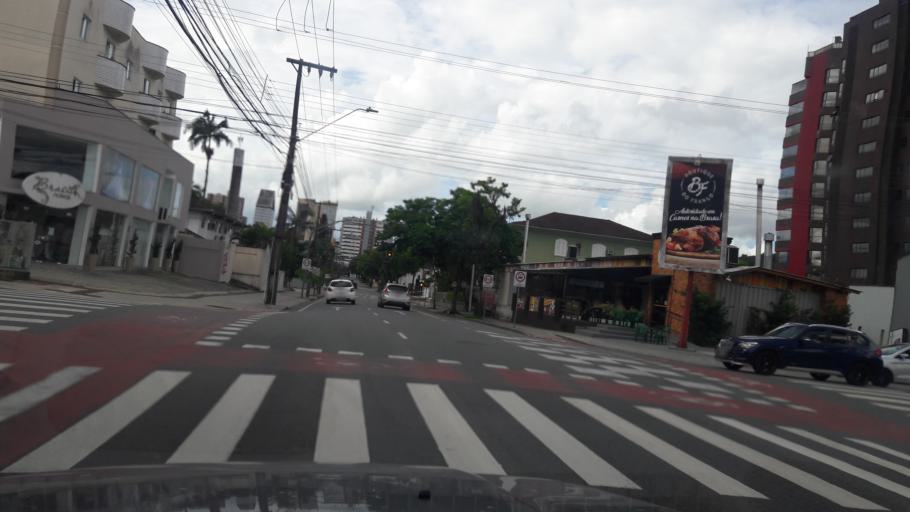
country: BR
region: Santa Catarina
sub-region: Joinville
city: Joinville
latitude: -26.3122
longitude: -48.8428
